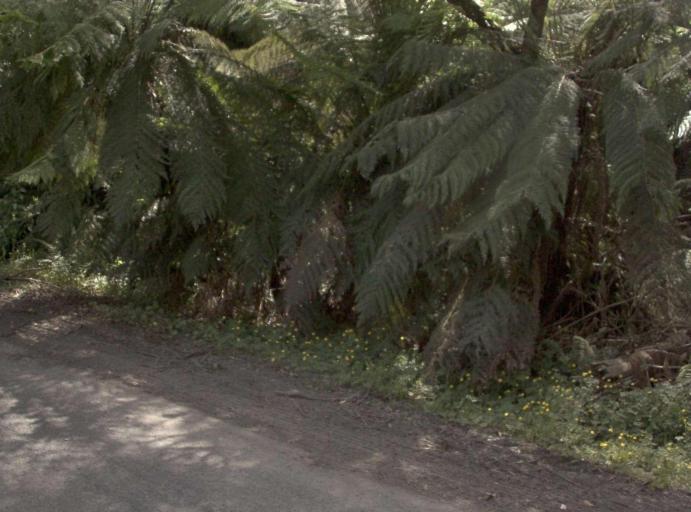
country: AU
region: Victoria
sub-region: Latrobe
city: Traralgon
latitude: -38.4220
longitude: 146.5701
